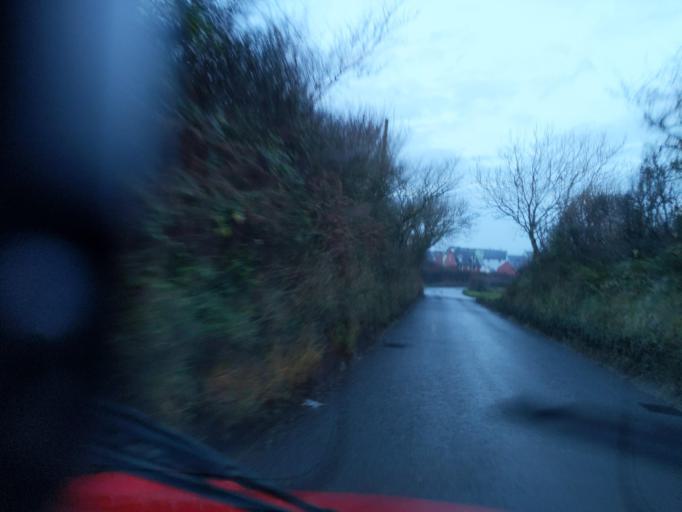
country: GB
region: England
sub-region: Plymouth
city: Plymstock
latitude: 50.3477
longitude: -4.0777
